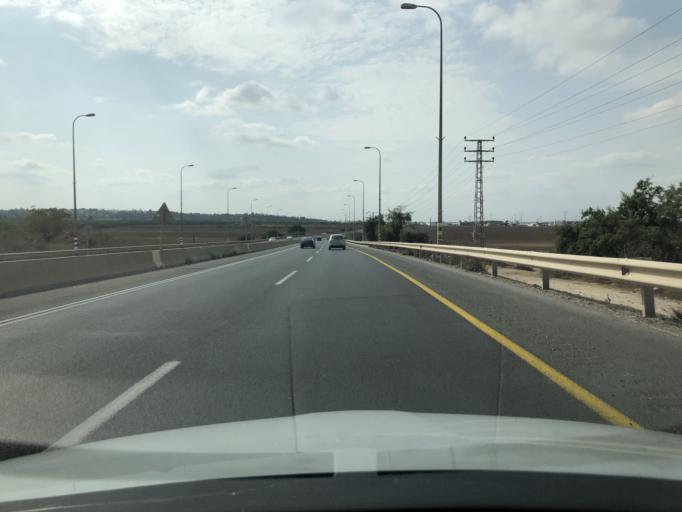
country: IL
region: Central District
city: Et Taiyiba
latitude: 32.2397
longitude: 34.9885
